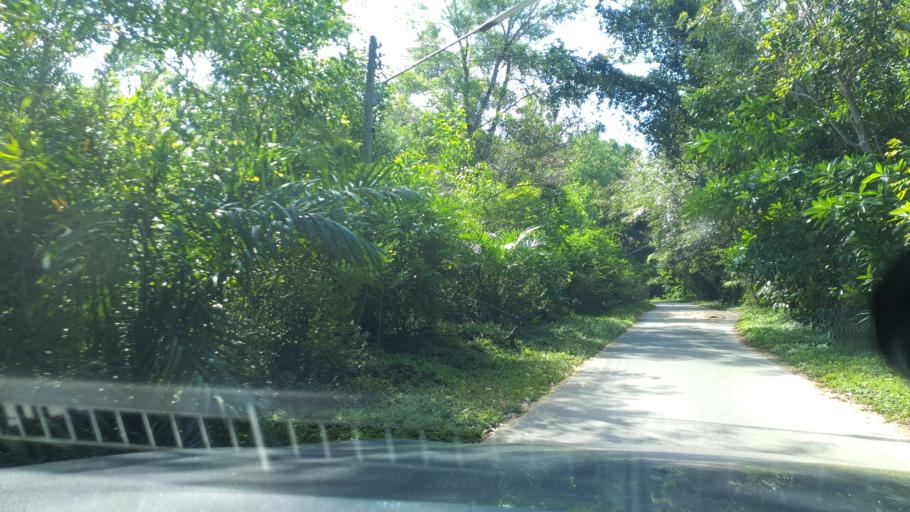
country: TH
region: Krabi
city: Krabi
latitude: 8.0240
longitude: 98.8790
